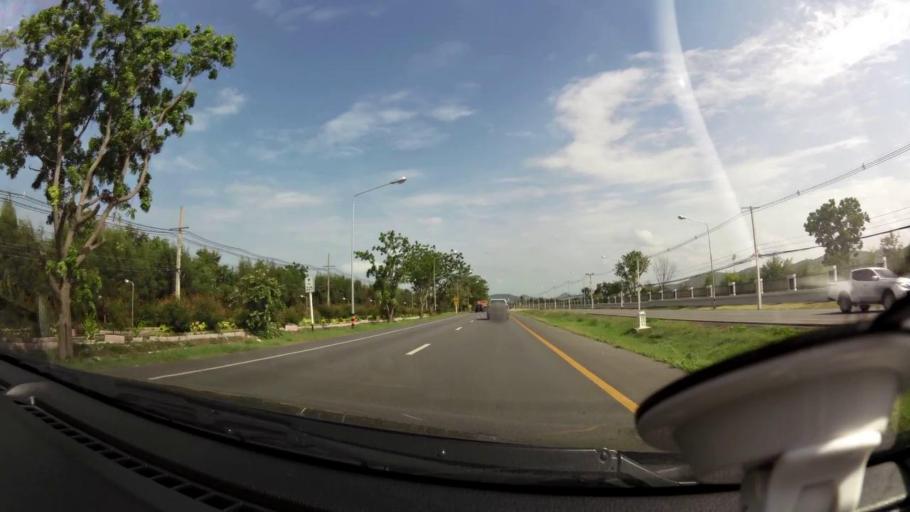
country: TH
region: Prachuap Khiri Khan
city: Hua Hin
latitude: 12.5064
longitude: 99.9677
